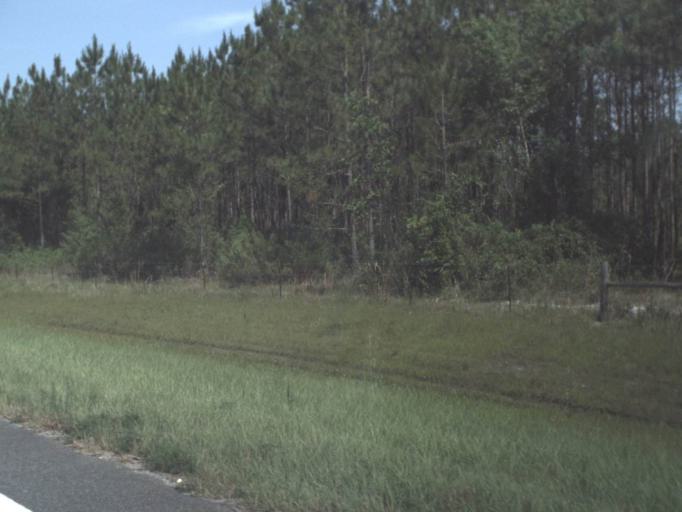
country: US
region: Florida
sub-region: Clay County
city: Middleburg
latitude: 29.9781
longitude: -81.8827
